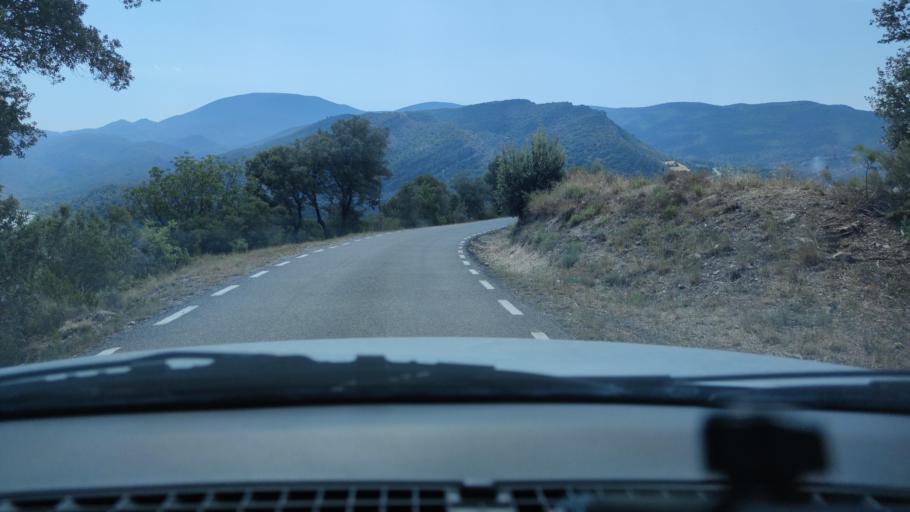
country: ES
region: Catalonia
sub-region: Provincia de Lleida
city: Ager
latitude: 42.0054
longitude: 0.8360
